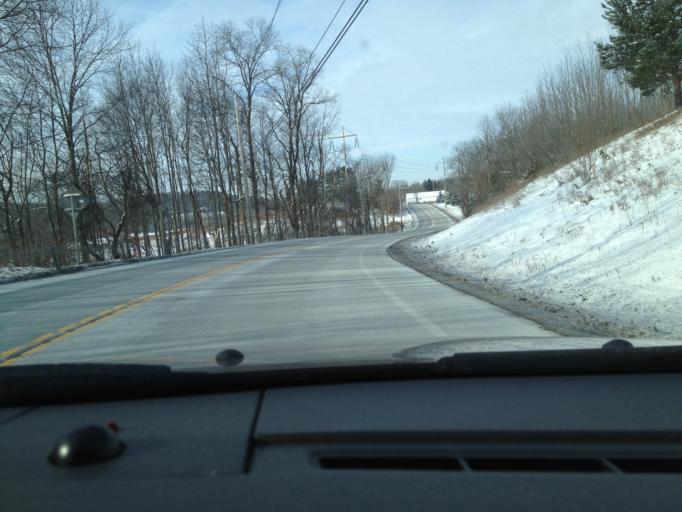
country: US
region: New York
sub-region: Rensselaer County
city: West Sand Lake
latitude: 42.6420
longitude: -73.6201
